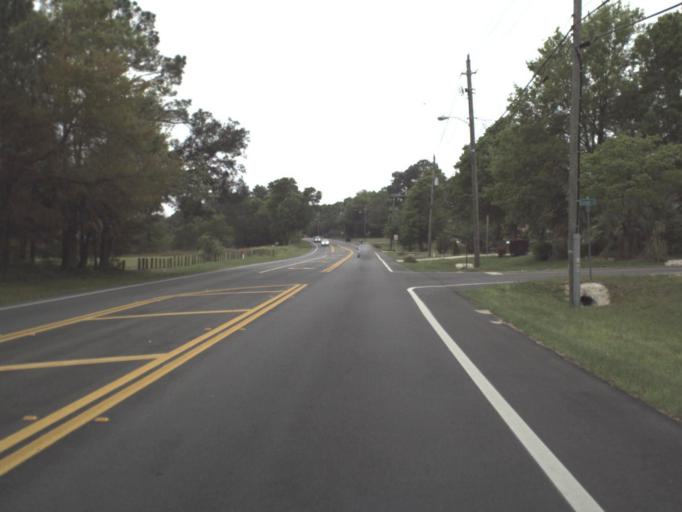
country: US
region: Florida
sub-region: Escambia County
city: East Pensacola Heights
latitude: 30.4483
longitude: -87.1726
